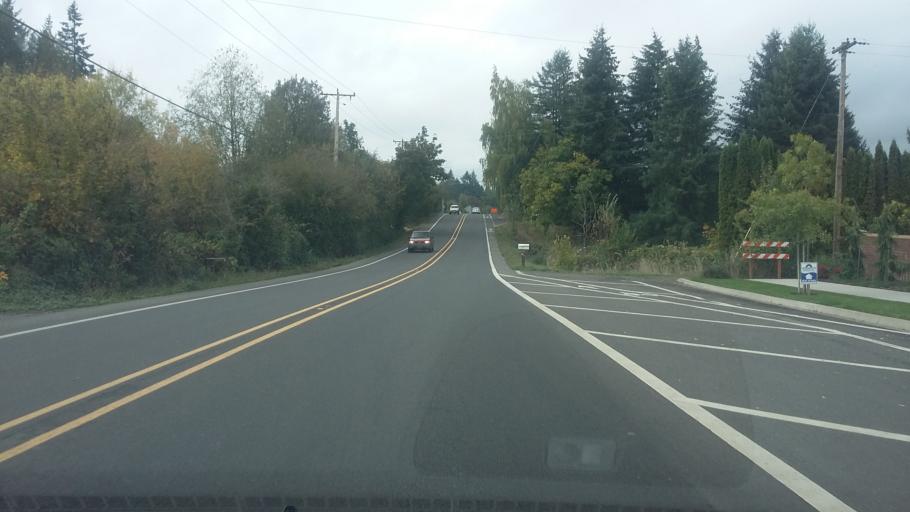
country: US
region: Washington
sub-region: Clark County
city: Ridgefield
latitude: 45.8157
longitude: -122.7101
